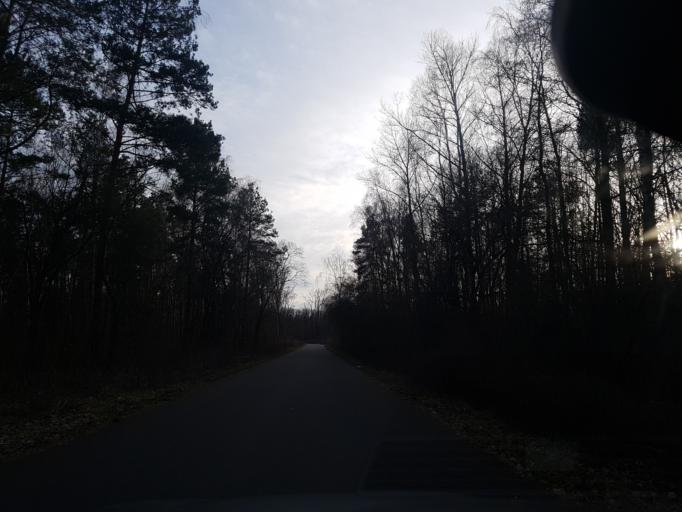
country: DE
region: Brandenburg
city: Trobitz
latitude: 51.5898
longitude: 13.4219
